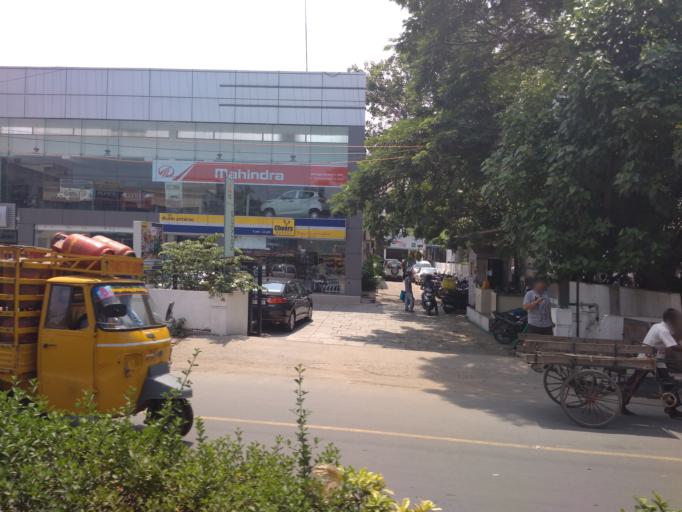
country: IN
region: Tamil Nadu
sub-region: Chennai
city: Gandhi Nagar
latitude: 13.0025
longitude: 80.2566
